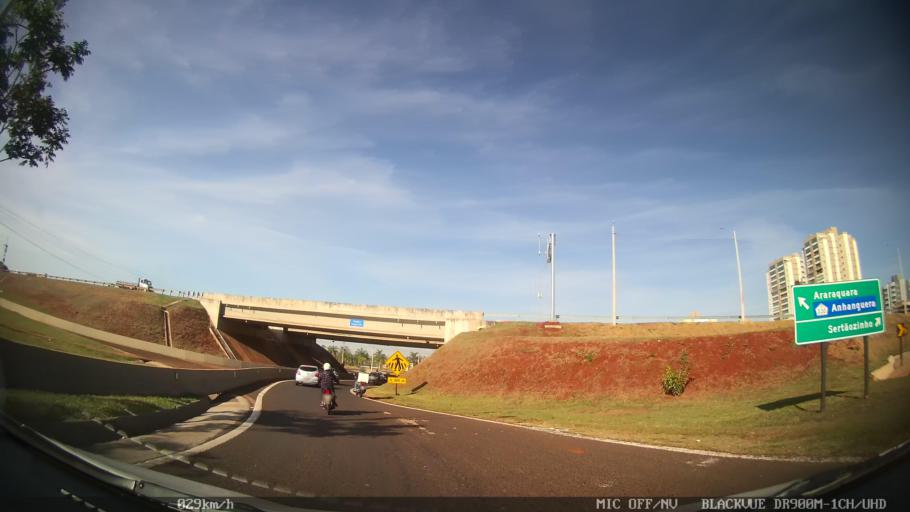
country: BR
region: Sao Paulo
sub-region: Ribeirao Preto
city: Ribeirao Preto
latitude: -21.2192
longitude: -47.8274
